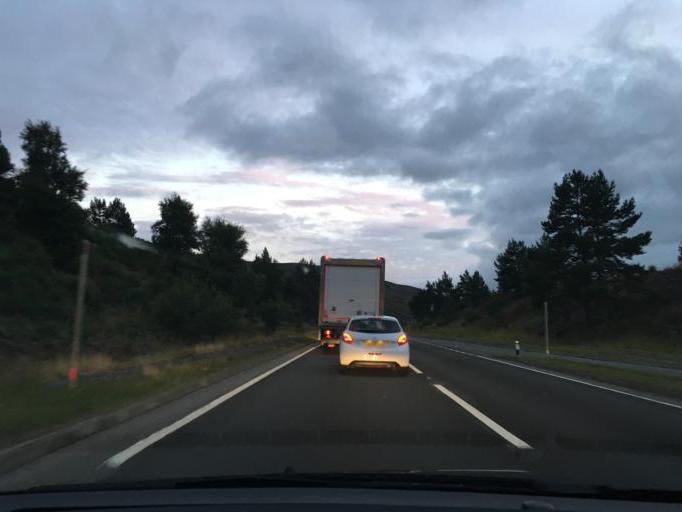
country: GB
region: Scotland
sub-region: Highland
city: Kingussie
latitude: 56.9872
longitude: -4.1774
